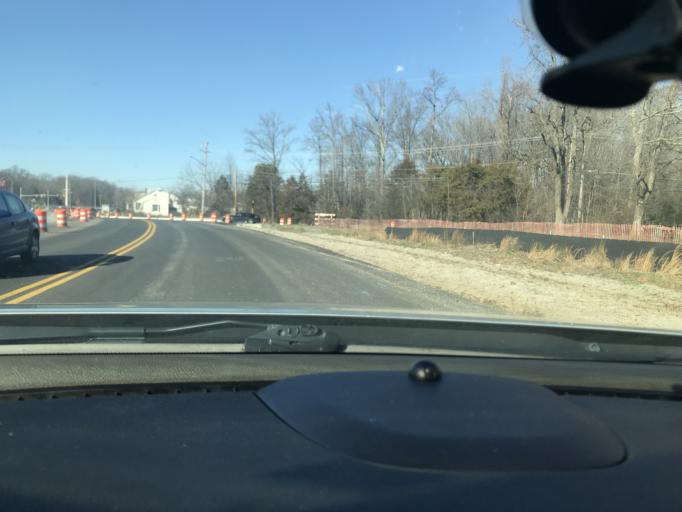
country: US
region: Maryland
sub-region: Prince George's County
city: Brandywine
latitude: 38.7013
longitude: -76.8725
